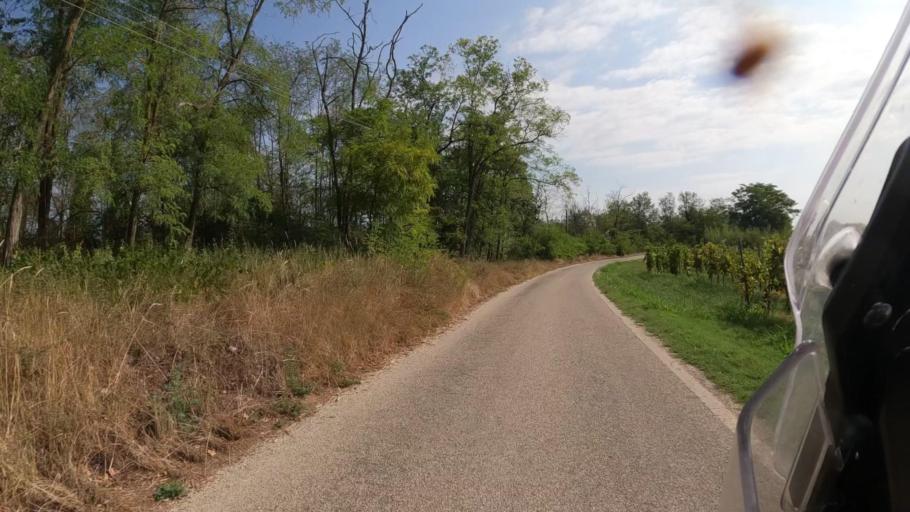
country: IT
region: Piedmont
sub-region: Provincia di Asti
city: Viarigi
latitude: 44.9584
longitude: 8.3749
